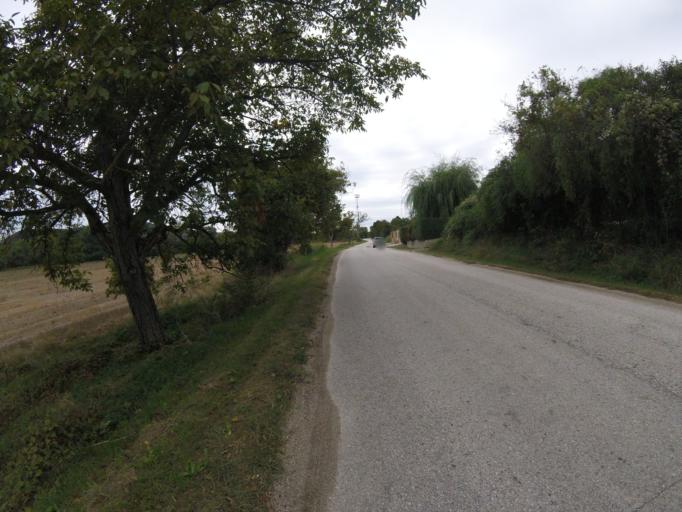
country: HU
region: Pest
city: Szob
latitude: 47.8269
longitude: 18.8057
